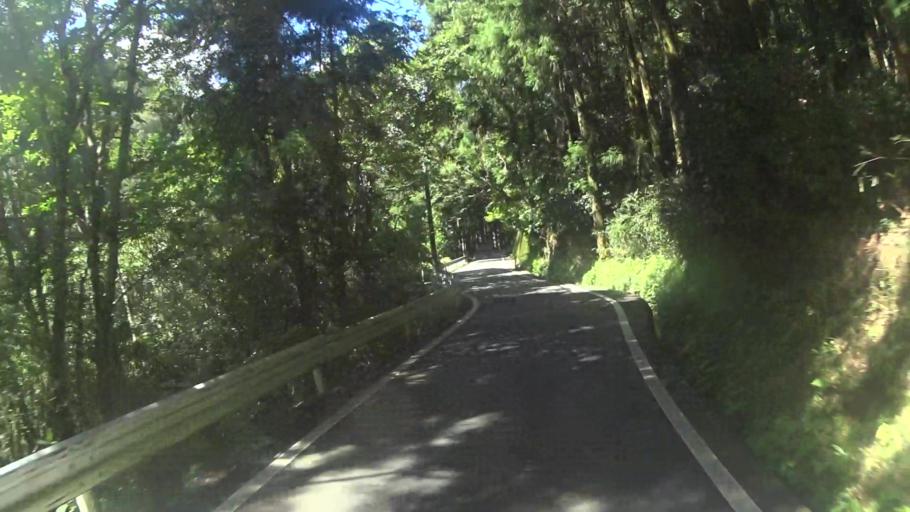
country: JP
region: Nara
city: Nara-shi
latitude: 34.7479
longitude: 135.9393
